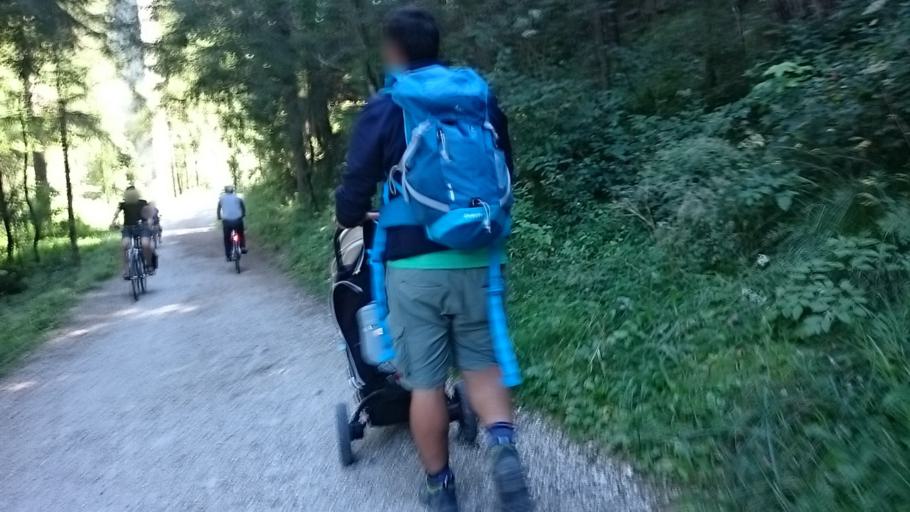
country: IT
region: Trentino-Alto Adige
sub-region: Bolzano
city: Riscone
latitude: 46.7891
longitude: 11.9509
